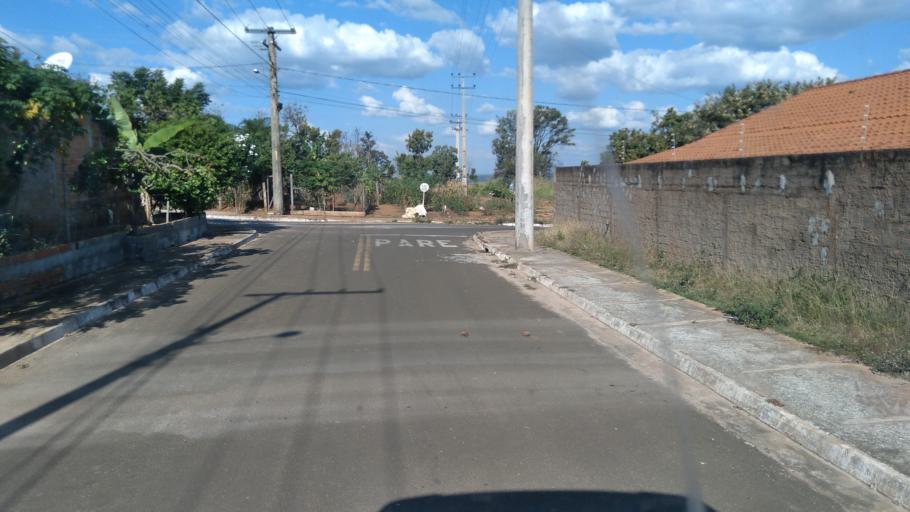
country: YE
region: Al Mahrah
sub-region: Shahan
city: Shihan as Sufla
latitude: 17.5502
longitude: 52.5389
